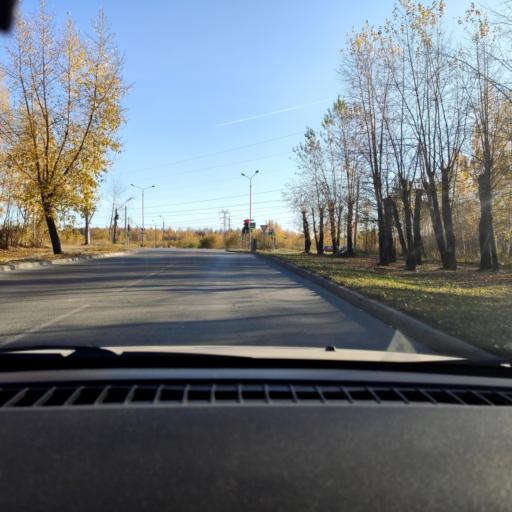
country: RU
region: Perm
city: Perm
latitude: 58.1019
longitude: 56.3891
